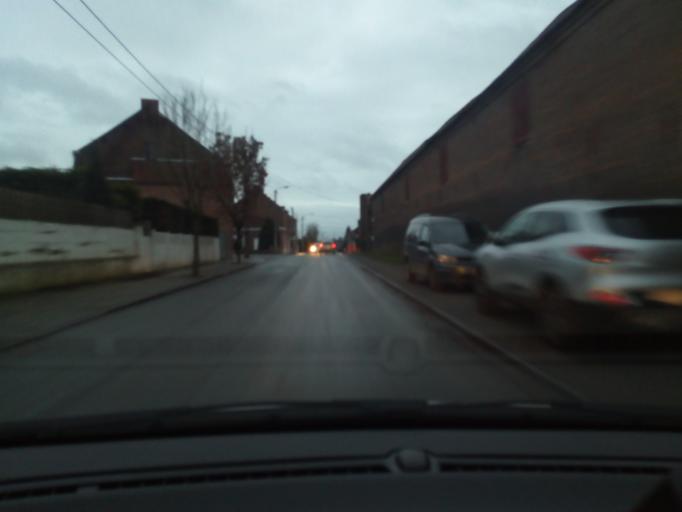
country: BE
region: Wallonia
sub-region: Province du Hainaut
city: Estinnes-au-Val
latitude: 50.4531
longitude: 4.0997
